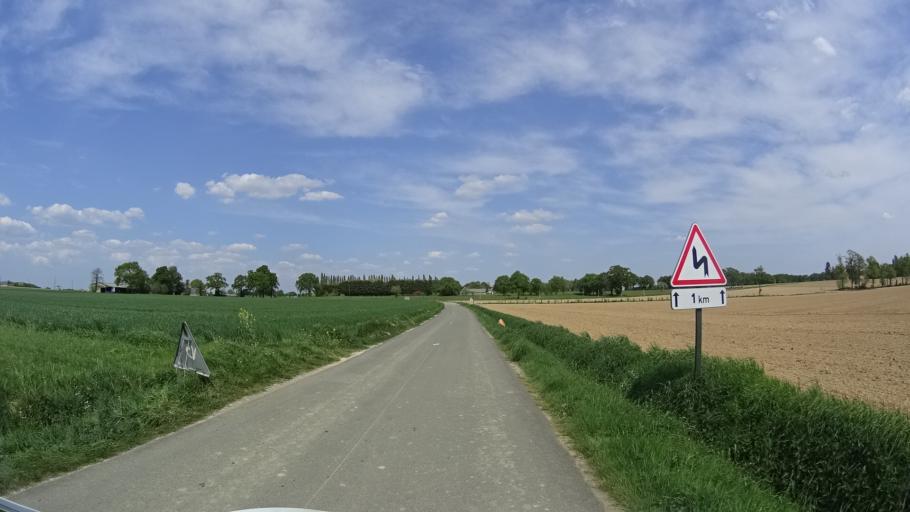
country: FR
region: Brittany
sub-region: Departement d'Ille-et-Vilaine
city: Torce
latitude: 48.0427
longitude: -1.2644
